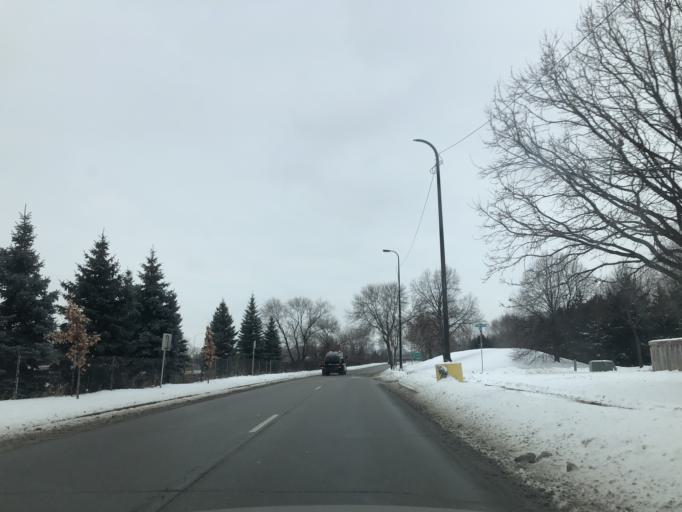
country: US
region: Minnesota
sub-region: Anoka County
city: Columbia Heights
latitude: 45.0497
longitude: -93.2854
